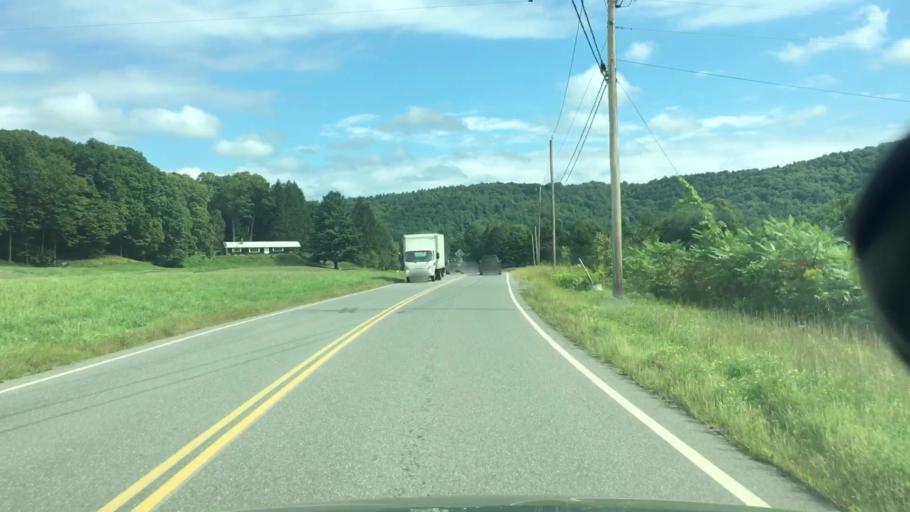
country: US
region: Massachusetts
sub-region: Franklin County
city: Colrain
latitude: 42.6783
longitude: -72.6949
